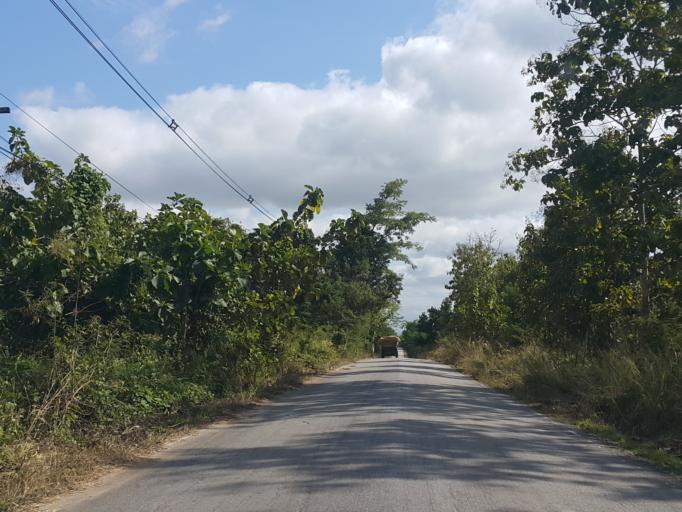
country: TH
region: Lampang
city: Hang Chat
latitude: 18.3388
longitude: 99.3807
